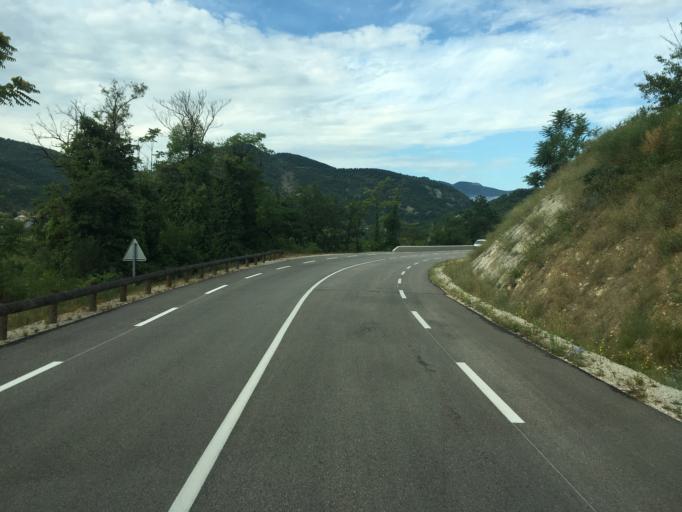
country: FR
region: Rhone-Alpes
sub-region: Departement de la Drome
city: Nyons
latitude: 44.4094
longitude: 5.2540
